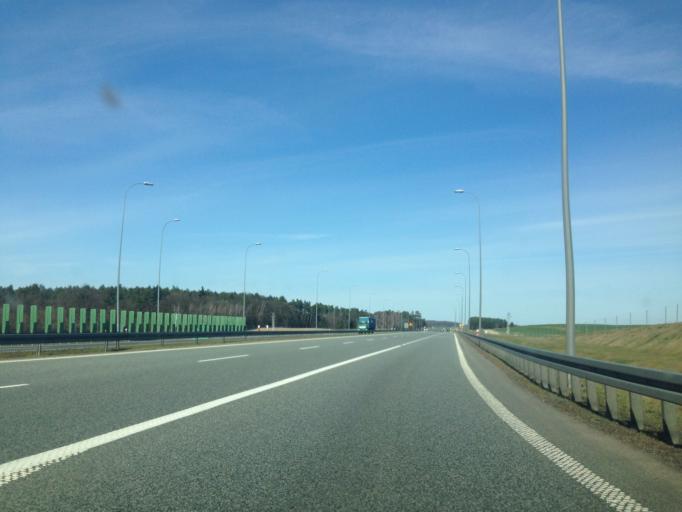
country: PL
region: Pomeranian Voivodeship
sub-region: Powiat starogardzki
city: Bobowo
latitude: 53.8887
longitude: 18.6315
